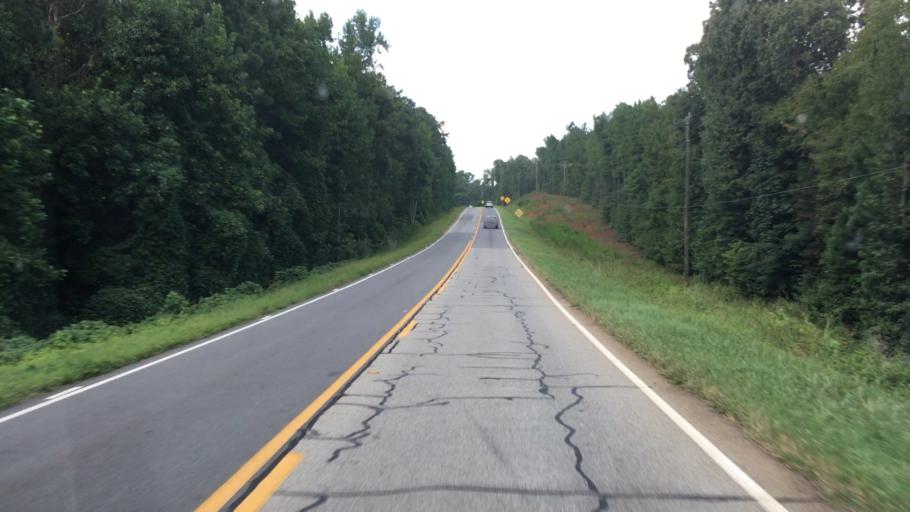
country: US
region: Georgia
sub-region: Jasper County
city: Monticello
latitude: 33.2568
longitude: -83.7187
